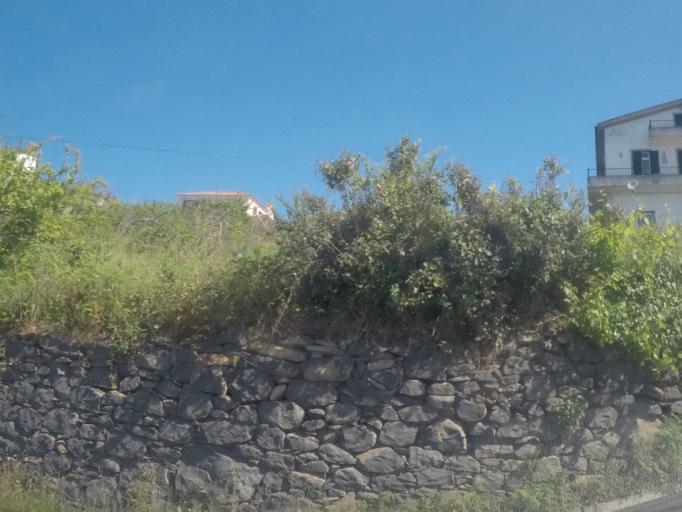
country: PT
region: Madeira
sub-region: Camara de Lobos
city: Curral das Freiras
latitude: 32.6823
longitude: -16.9698
